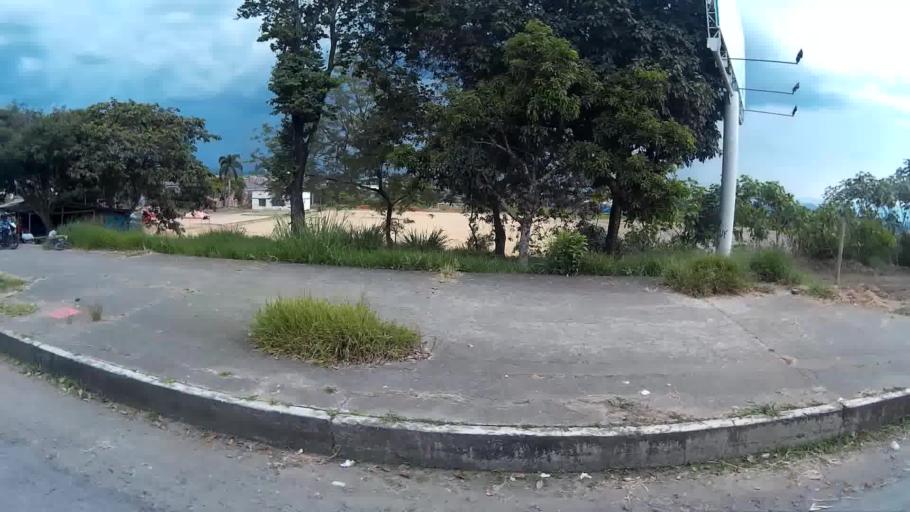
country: CO
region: Risaralda
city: Pereira
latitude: 4.8100
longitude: -75.7514
